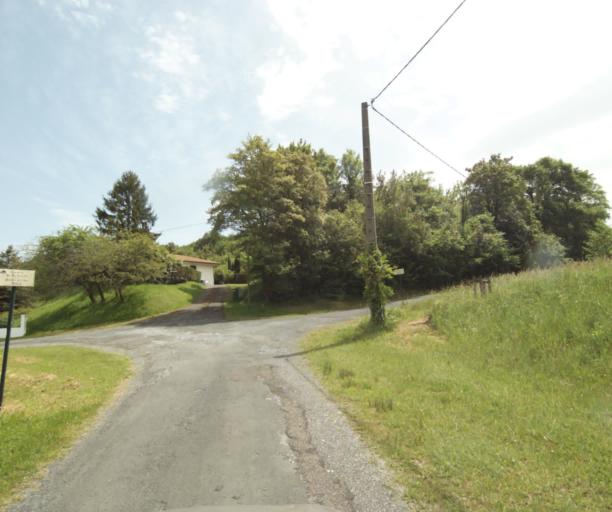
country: FR
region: Aquitaine
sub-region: Departement des Pyrenees-Atlantiques
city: Mouguerre
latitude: 43.4835
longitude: -1.4309
